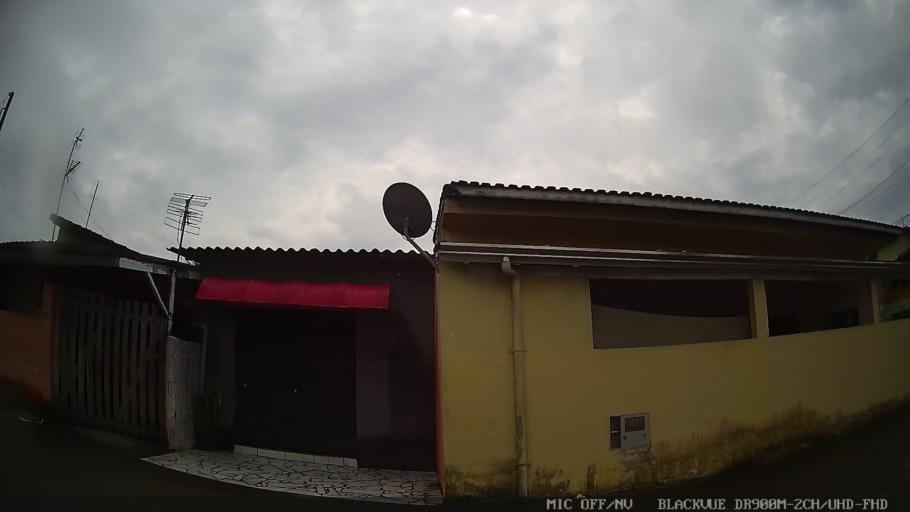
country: BR
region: Sao Paulo
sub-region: Sao Sebastiao
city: Sao Sebastiao
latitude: -23.6953
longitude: -45.4454
